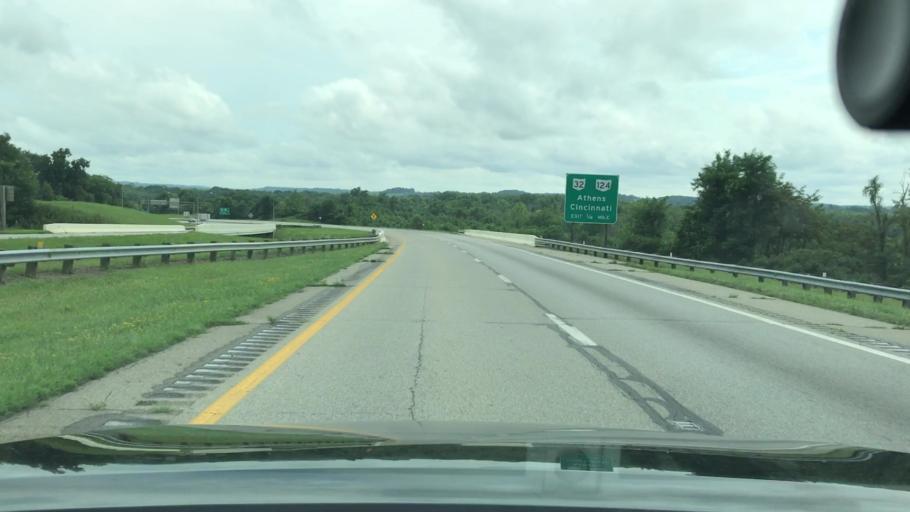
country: US
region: Ohio
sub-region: Jackson County
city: Jackson
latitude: 39.0537
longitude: -82.6183
